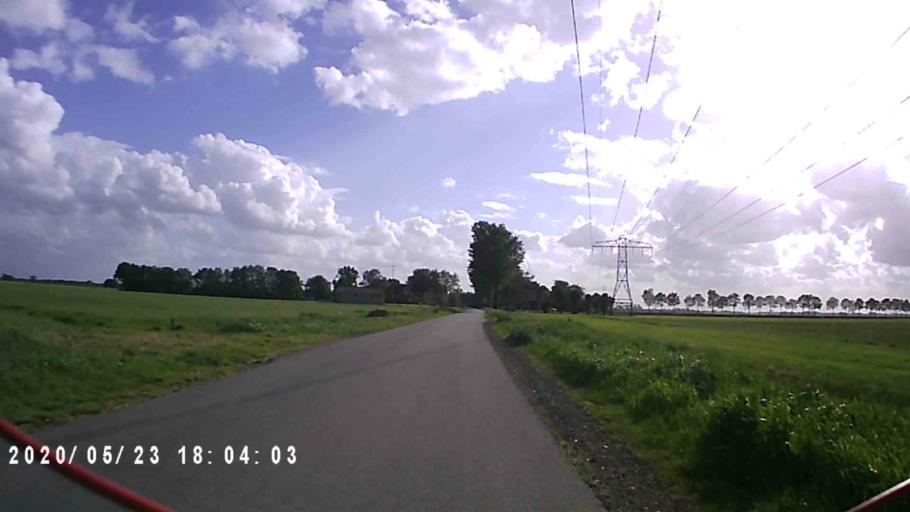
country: NL
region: Groningen
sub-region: Gemeente Slochteren
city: Slochteren
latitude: 53.2438
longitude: 6.7233
